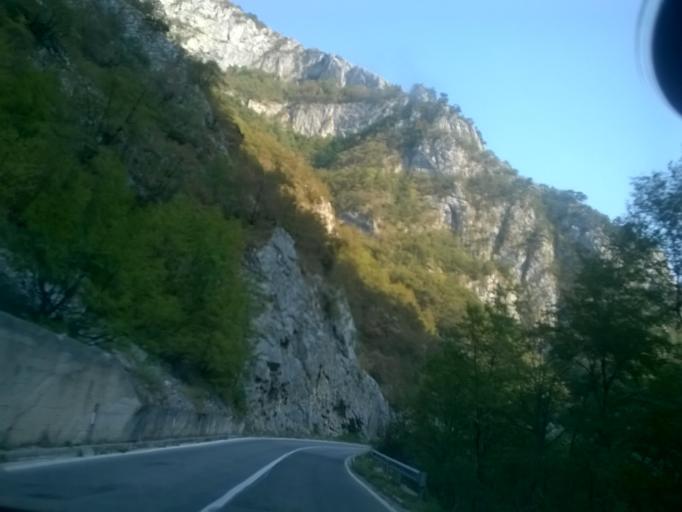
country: ME
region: Opstina Pluzine
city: Pluzine
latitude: 43.2298
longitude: 18.8461
